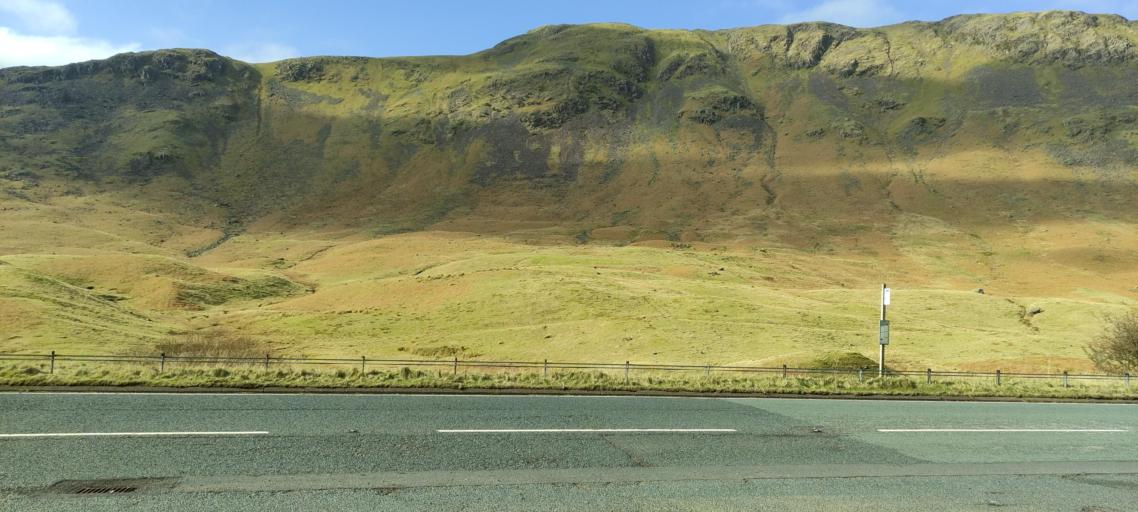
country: GB
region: England
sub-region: Cumbria
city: Ambleside
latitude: 54.4911
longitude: -3.0363
